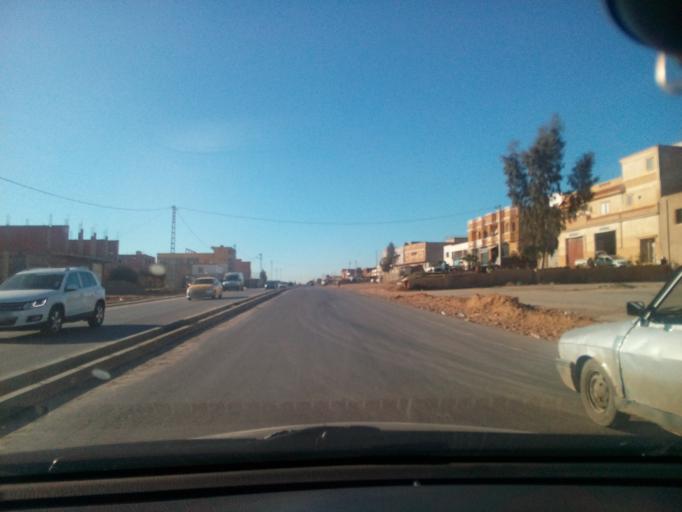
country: DZ
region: Mostaganem
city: Mostaganem
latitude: 35.9096
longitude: 0.1614
